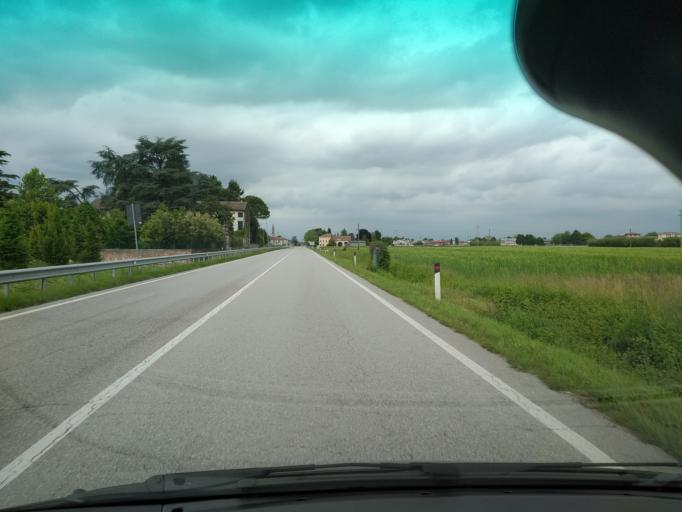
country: IT
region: Veneto
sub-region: Provincia di Padova
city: Tremignon
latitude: 45.5138
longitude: 11.8093
